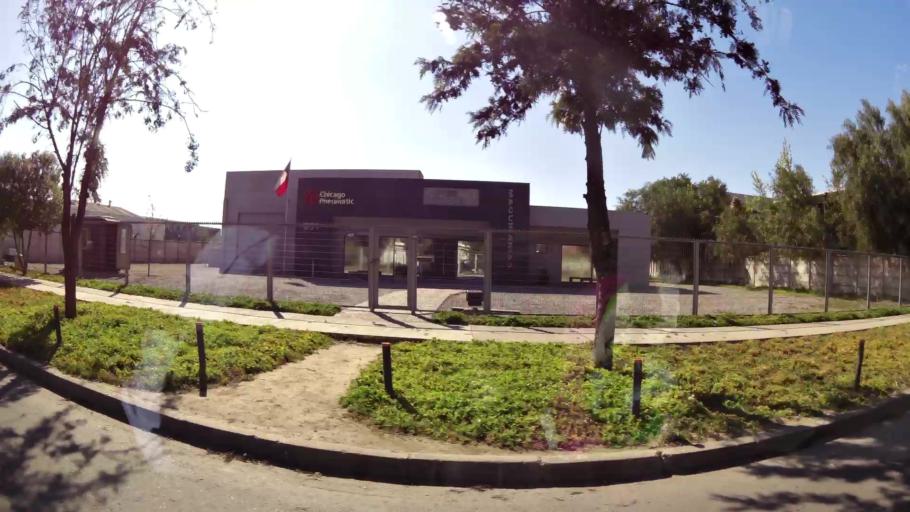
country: CL
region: Santiago Metropolitan
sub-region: Provincia de Chacabuco
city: Chicureo Abajo
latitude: -33.3303
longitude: -70.7097
